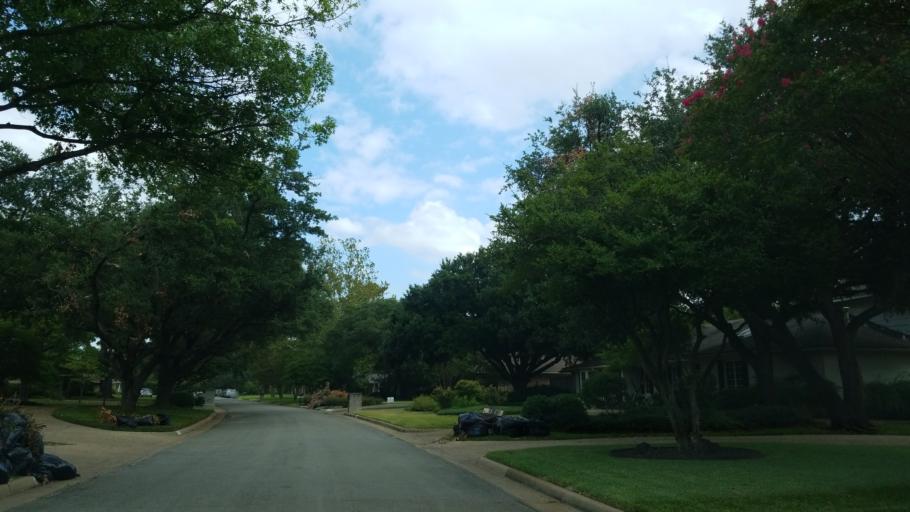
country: US
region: Texas
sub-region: Dallas County
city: Addison
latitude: 32.9467
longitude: -96.7846
